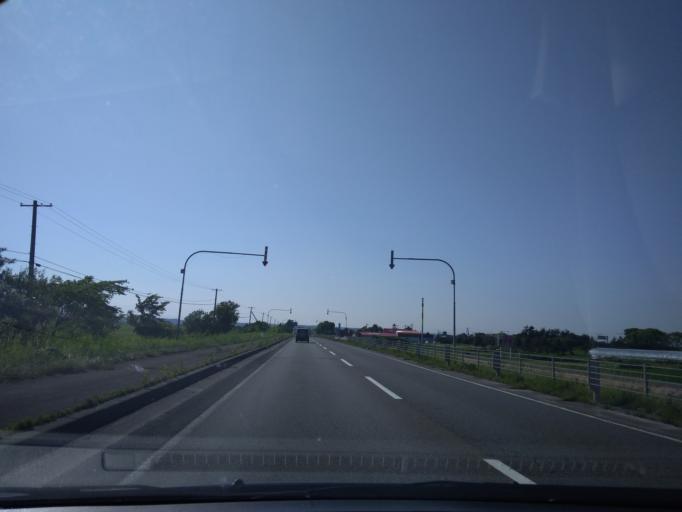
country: JP
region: Hokkaido
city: Kitahiroshima
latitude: 42.9945
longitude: 141.5959
